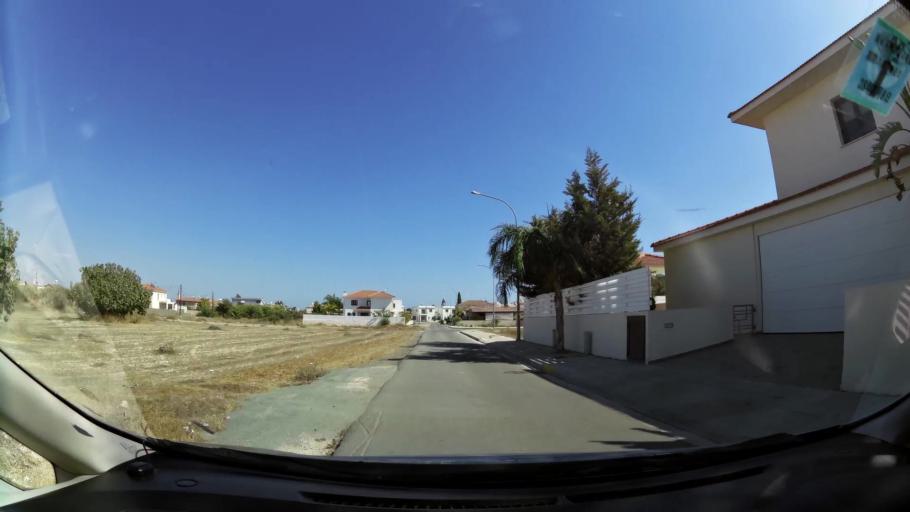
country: CY
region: Larnaka
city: Livadia
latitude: 34.9544
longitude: 33.6218
